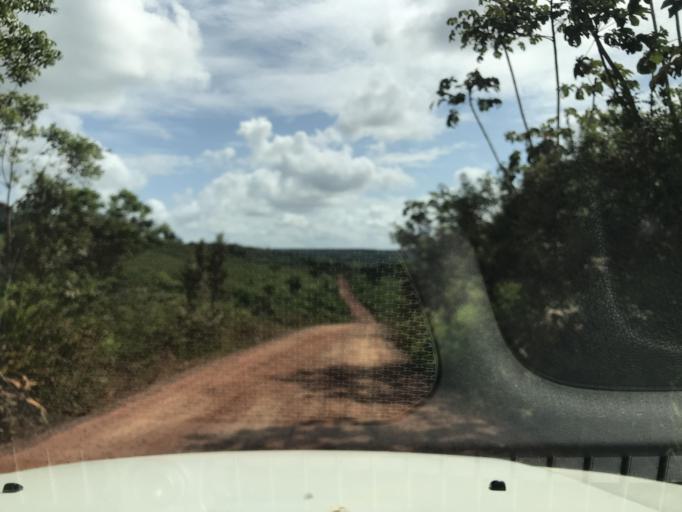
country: BR
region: Bahia
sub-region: Entre Rios
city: Entre Rios
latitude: -12.1705
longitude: -38.0970
